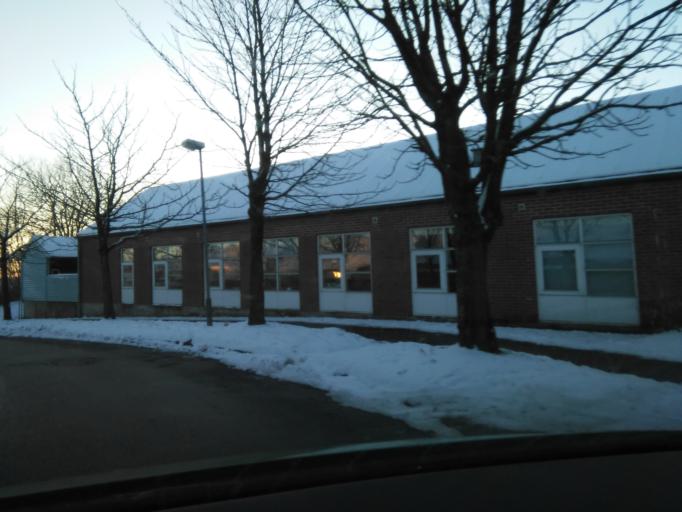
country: DK
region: Central Jutland
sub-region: Arhus Kommune
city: Kolt
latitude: 56.1103
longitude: 10.0781
